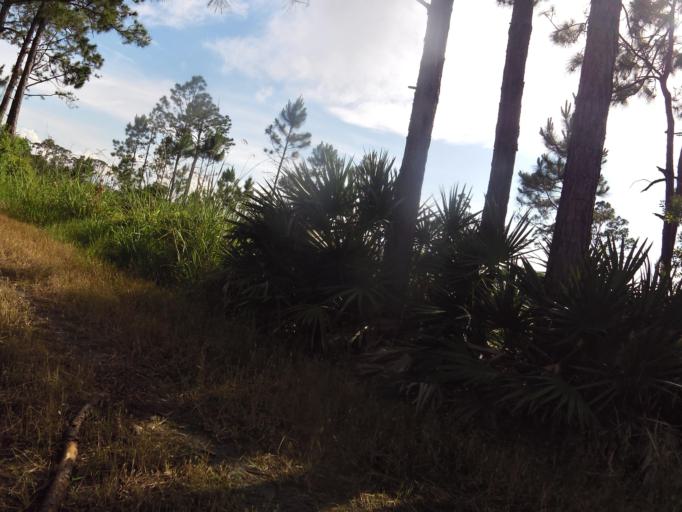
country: US
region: Florida
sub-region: Saint Johns County
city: Villano Beach
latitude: 30.0278
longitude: -81.3440
